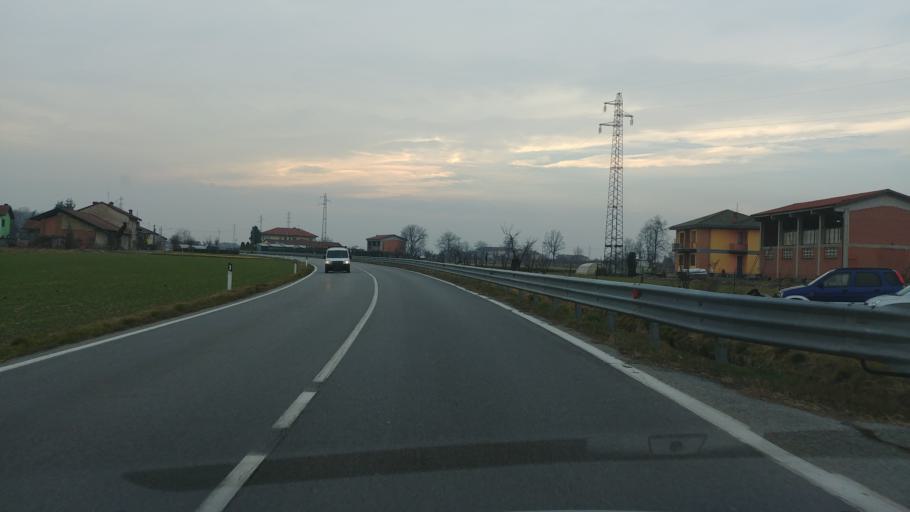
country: IT
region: Piedmont
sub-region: Provincia di Cuneo
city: Montanera
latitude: 44.4924
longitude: 7.6608
